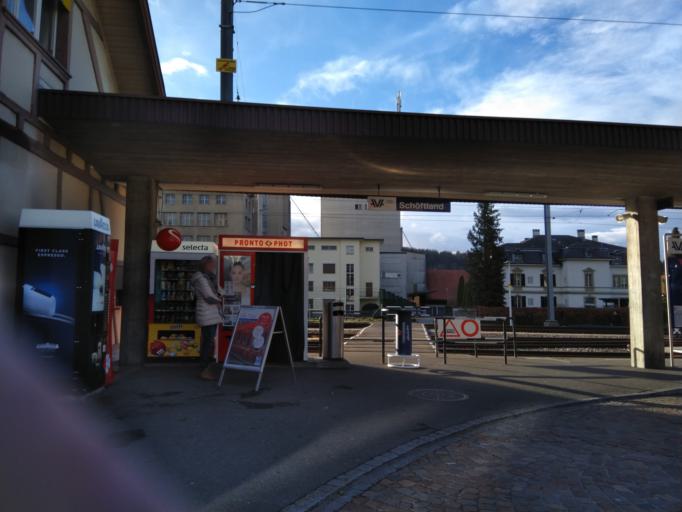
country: CH
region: Aargau
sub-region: Bezirk Kulm
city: Schoftland
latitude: 47.3055
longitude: 8.0501
